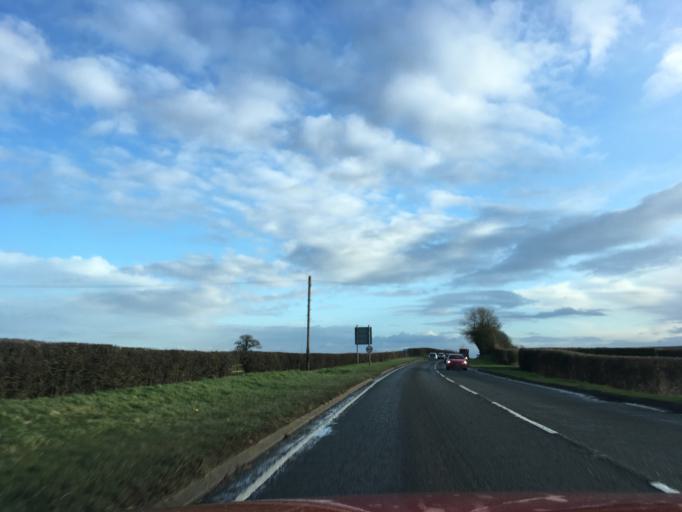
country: GB
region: England
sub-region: Warwickshire
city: Stratford-upon-Avon
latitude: 52.2225
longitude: -1.7350
